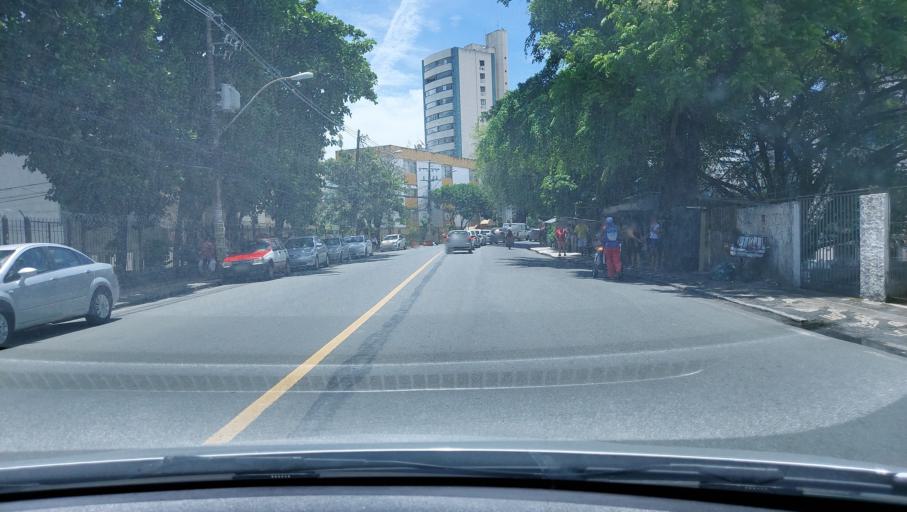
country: BR
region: Bahia
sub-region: Salvador
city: Salvador
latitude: -12.9906
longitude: -38.4836
